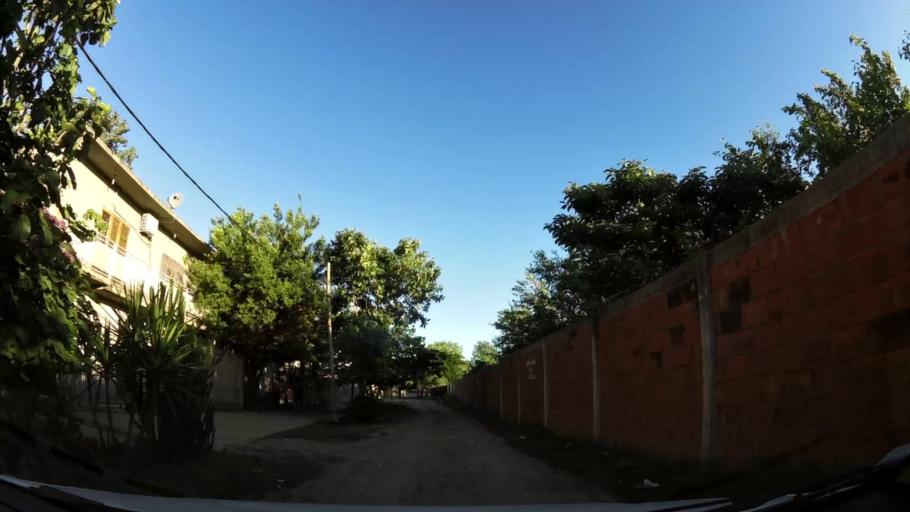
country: AR
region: Buenos Aires
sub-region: Partido de Moron
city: Moron
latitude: -34.7168
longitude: -58.6149
